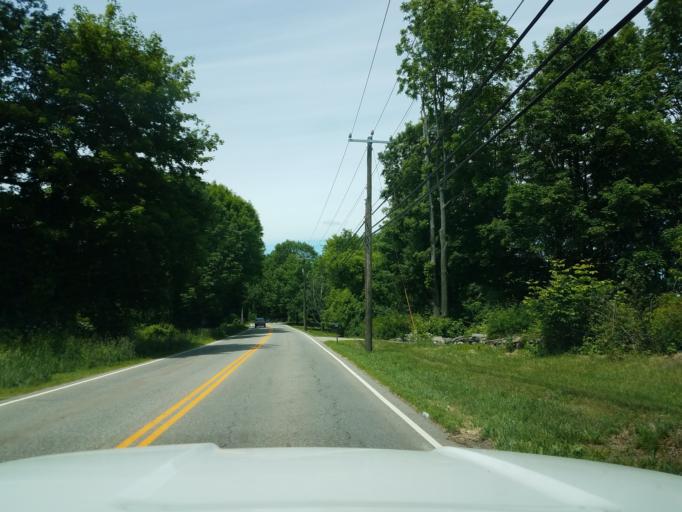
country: US
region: Connecticut
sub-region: Windham County
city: South Windham
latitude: 41.6295
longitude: -72.2016
